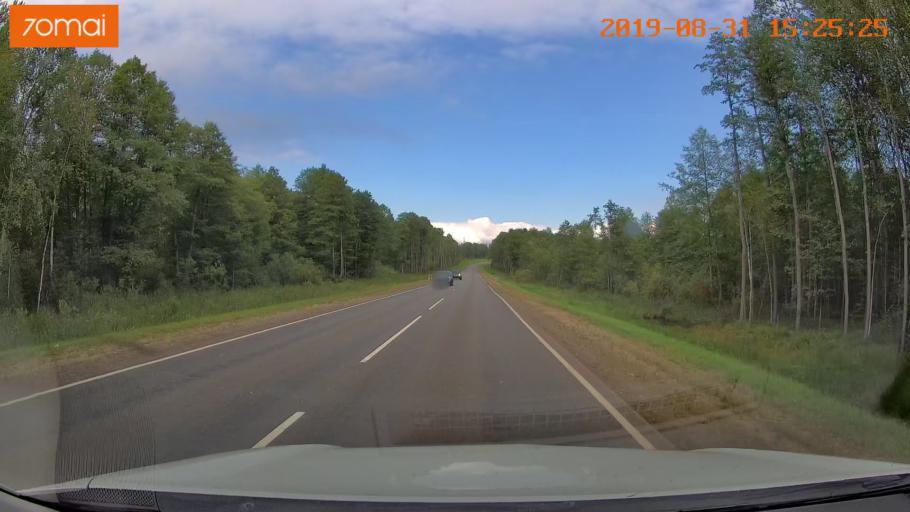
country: RU
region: Kaluga
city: Baryatino
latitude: 54.5412
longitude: 34.5194
